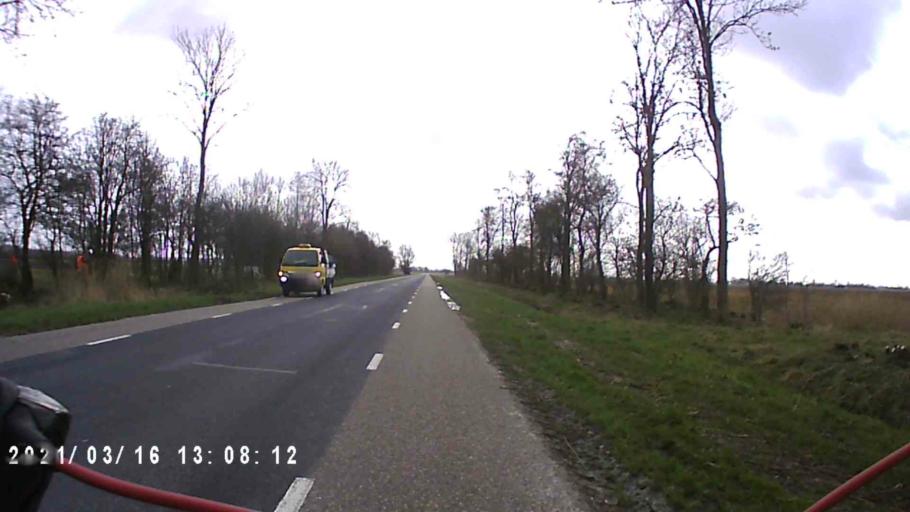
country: NL
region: Friesland
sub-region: Gemeente Het Bildt
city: Minnertsga
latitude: 53.2495
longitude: 5.6222
